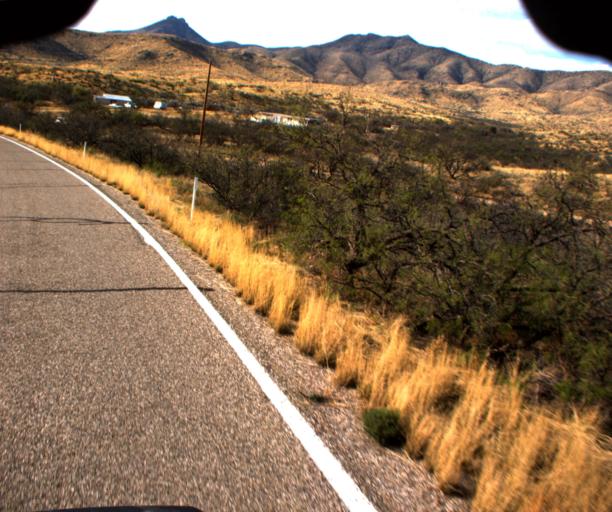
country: US
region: Arizona
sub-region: Cochise County
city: Willcox
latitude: 32.1587
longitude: -109.5662
